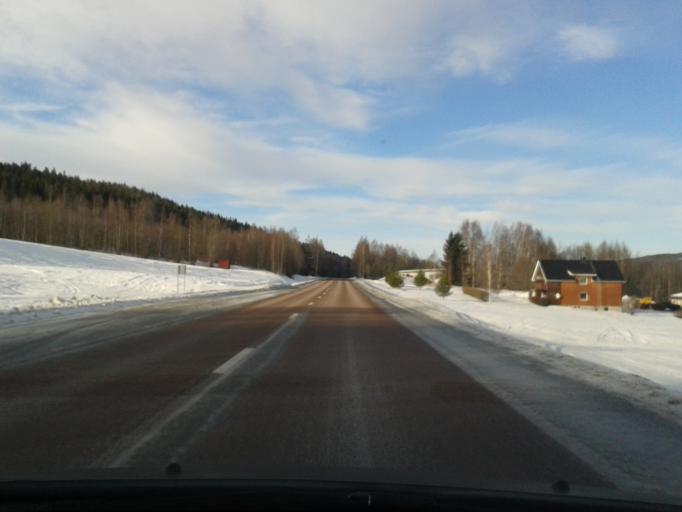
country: SE
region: Vaesternorrland
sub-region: OErnskoeldsviks Kommun
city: Bjasta
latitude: 63.3387
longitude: 18.5098
